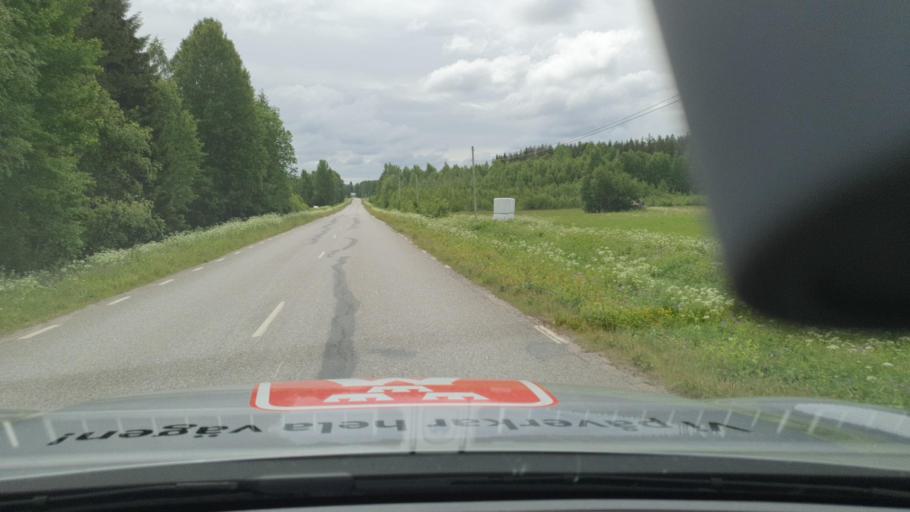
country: SE
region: Norrbotten
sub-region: Lulea Kommun
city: Ranea
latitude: 65.9272
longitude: 22.1442
